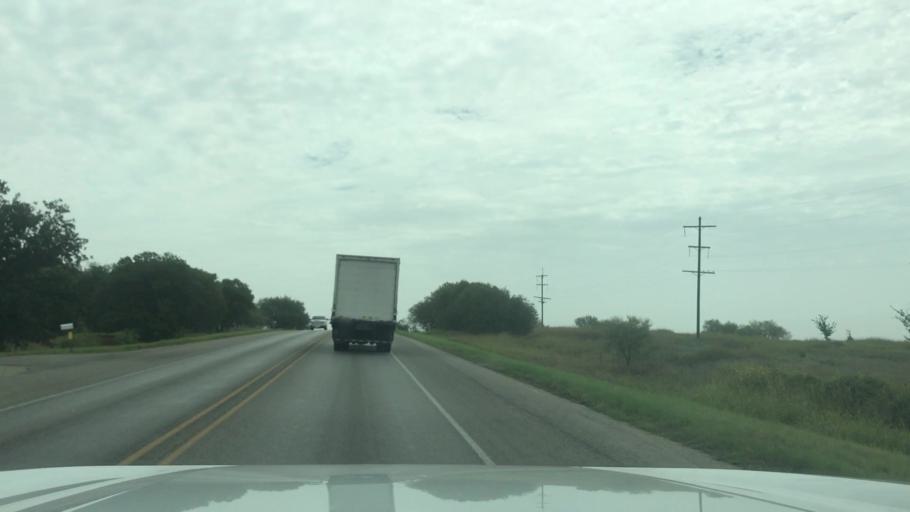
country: US
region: Texas
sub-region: Comanche County
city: De Leon
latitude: 32.1009
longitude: -98.4754
